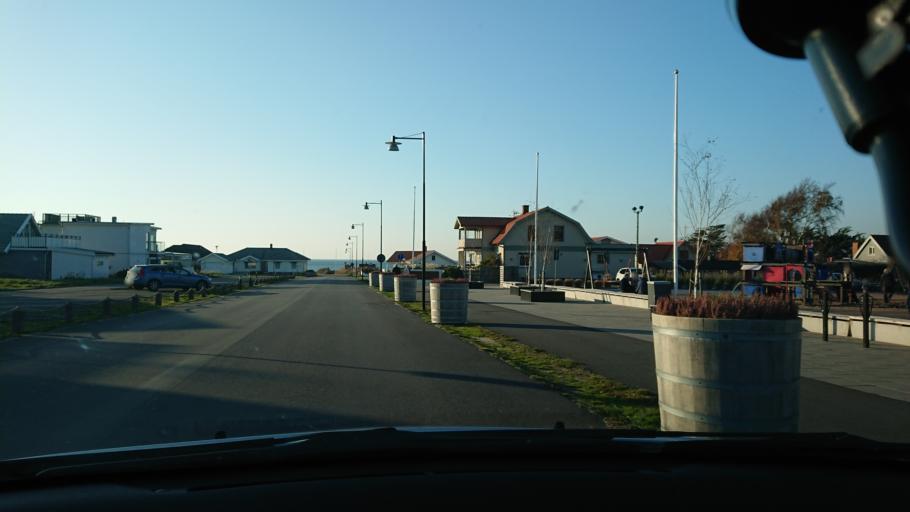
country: SE
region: Halland
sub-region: Laholms Kommun
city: Mellbystrand
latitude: 56.4618
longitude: 12.9185
